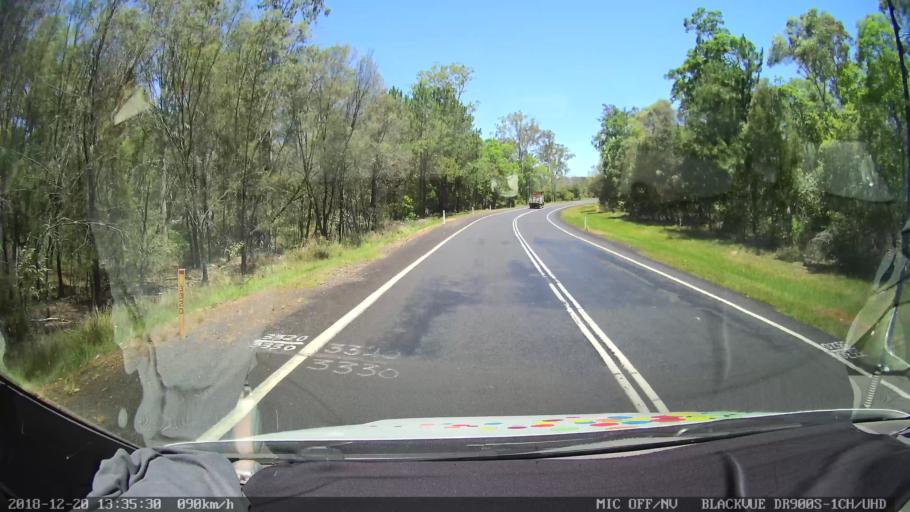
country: AU
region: New South Wales
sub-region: Clarence Valley
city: Gordon
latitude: -29.2701
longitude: 152.9919
